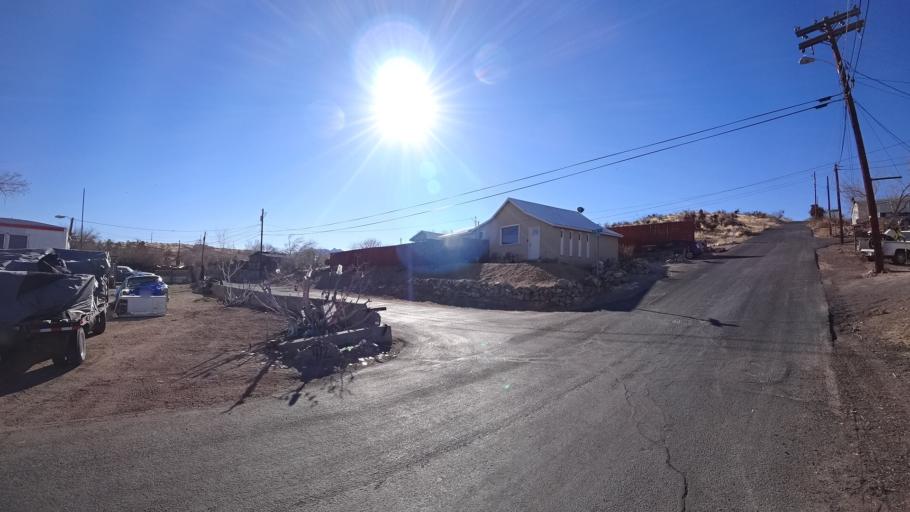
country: US
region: Arizona
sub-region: Mohave County
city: Kingman
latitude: 35.1847
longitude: -114.0520
